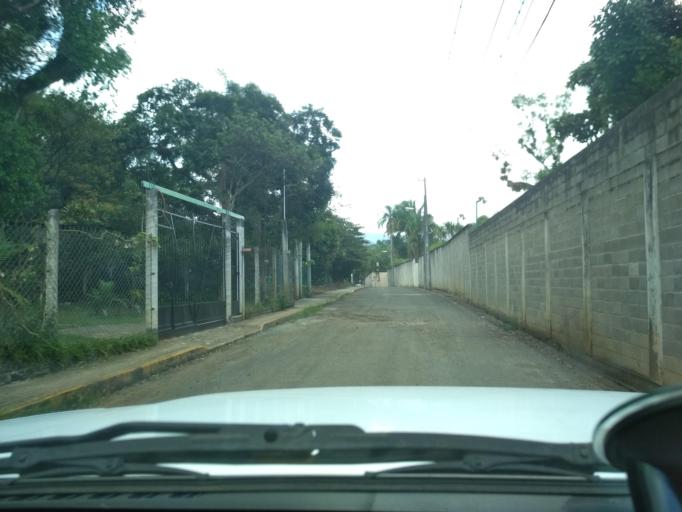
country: MX
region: Veracruz
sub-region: Cordoba
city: San Jose de Abajo [Unidad Habitacional]
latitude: 18.9176
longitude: -96.9544
